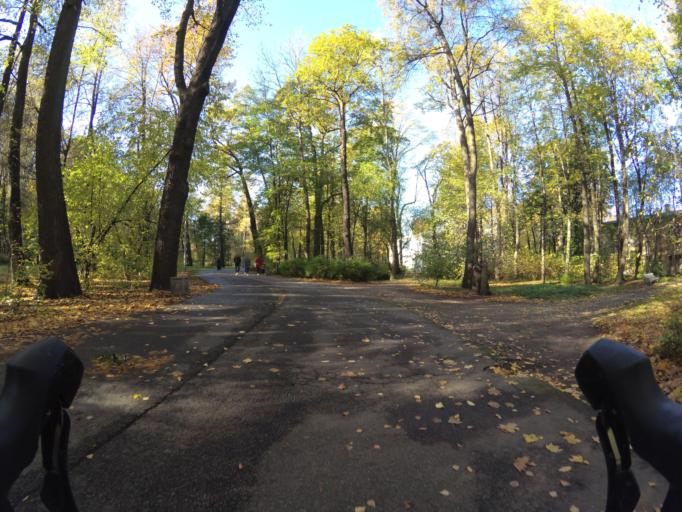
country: RU
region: Leningrad
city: Krestovskiy ostrov
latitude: 59.9797
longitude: 30.2639
